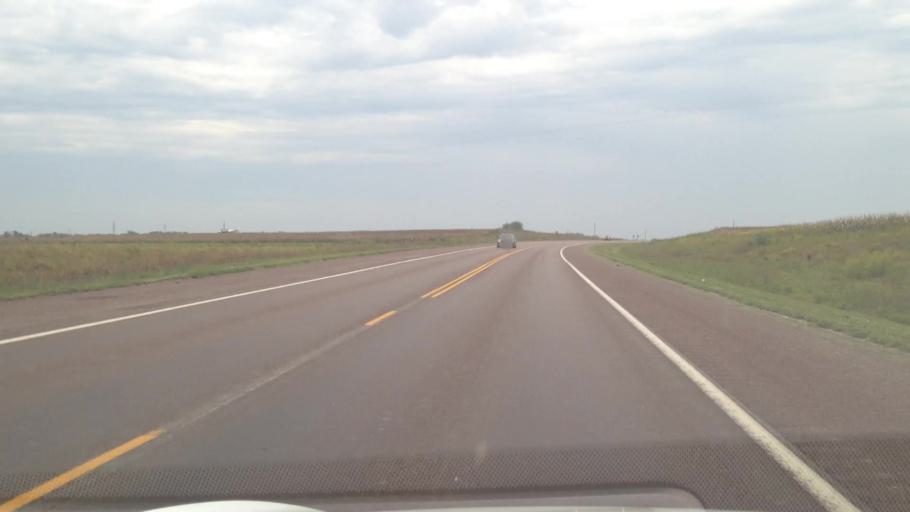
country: US
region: Kansas
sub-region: Crawford County
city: Girard
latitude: 37.4736
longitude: -94.8373
